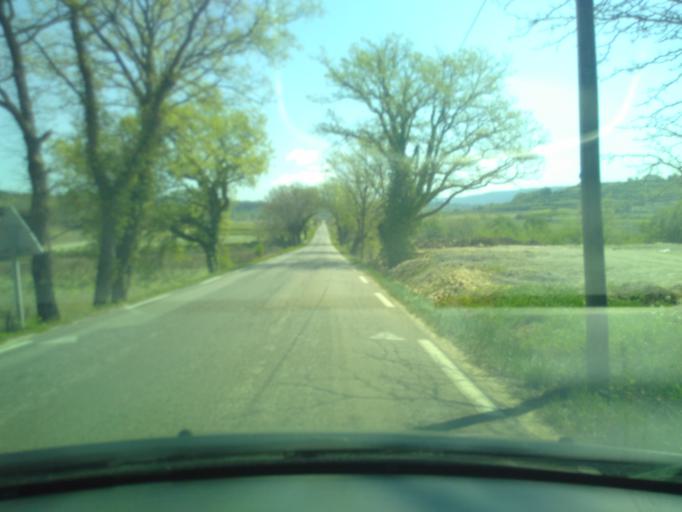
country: FR
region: Provence-Alpes-Cote d'Azur
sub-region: Departement du Vaucluse
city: Malemort-du-Comtat
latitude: 44.0233
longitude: 5.1390
